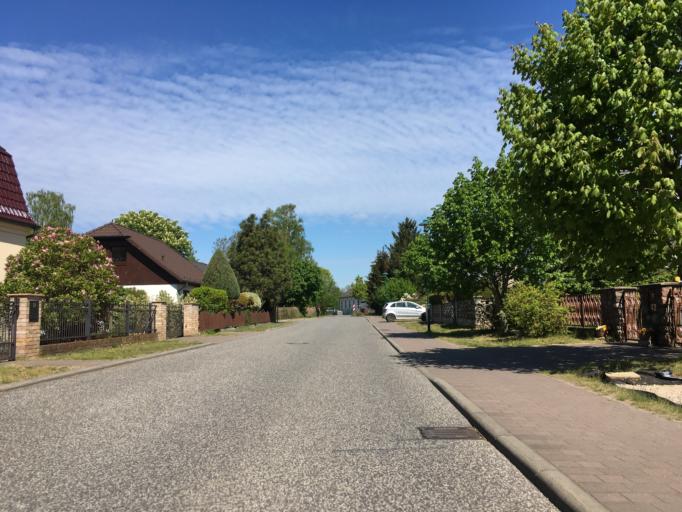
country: DE
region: Berlin
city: Buch
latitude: 52.6726
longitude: 13.5307
